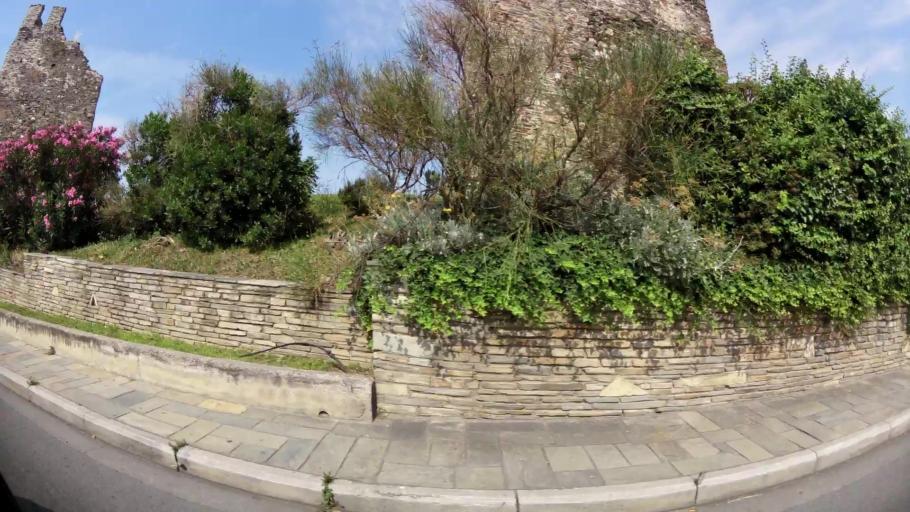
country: GR
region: Central Macedonia
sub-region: Nomos Thessalonikis
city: Agios Pavlos
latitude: 40.6432
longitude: 22.9632
